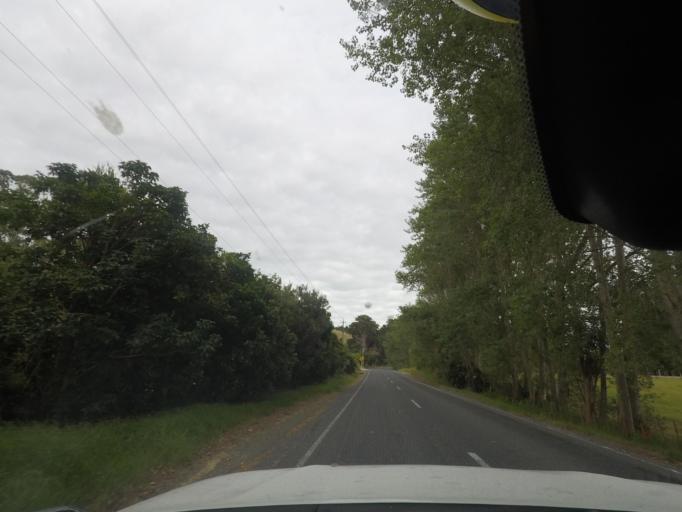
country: NZ
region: Auckland
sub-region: Auckland
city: Parakai
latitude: -36.5264
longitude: 174.2910
